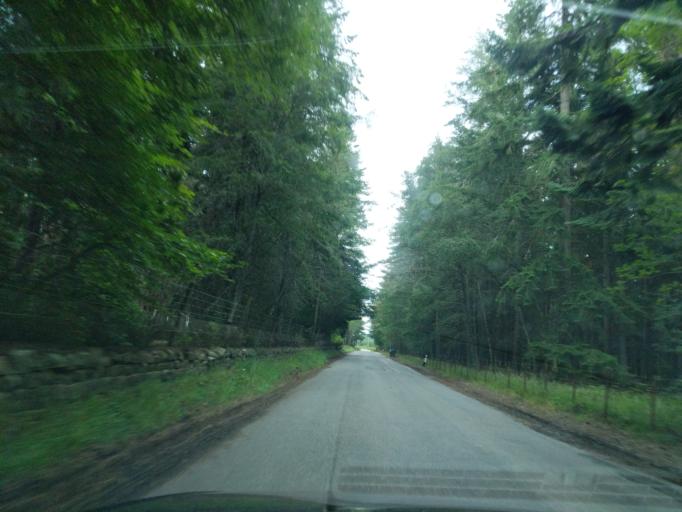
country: GB
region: Scotland
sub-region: Aberdeenshire
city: Aboyne
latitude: 57.0723
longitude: -2.8804
